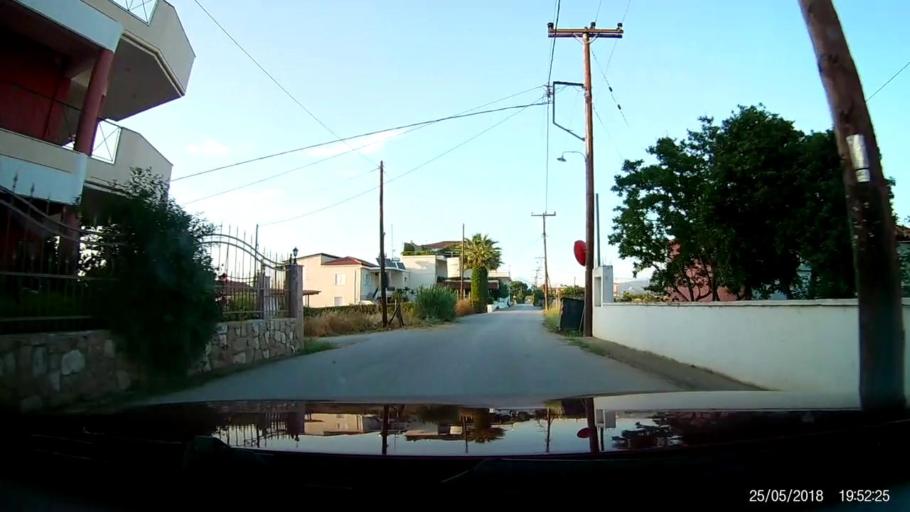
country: GR
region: Central Greece
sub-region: Nomos Evvoias
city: Ayios Nikolaos
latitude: 38.4110
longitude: 23.6453
